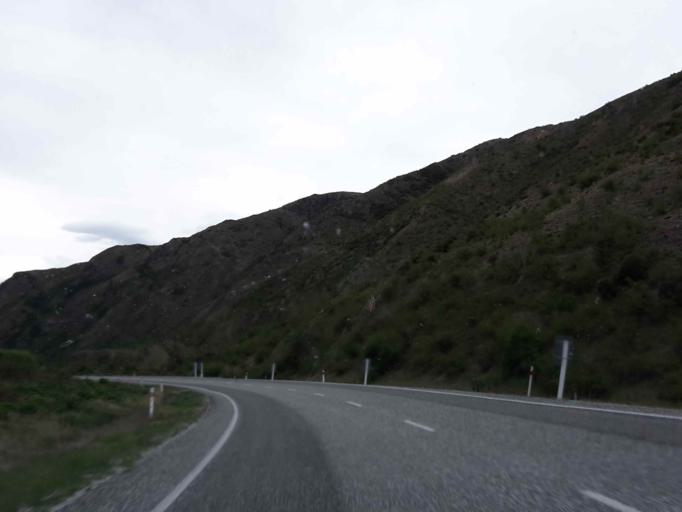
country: NZ
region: Otago
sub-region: Queenstown-Lakes District
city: Wanaka
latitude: -44.6297
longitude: 169.5193
